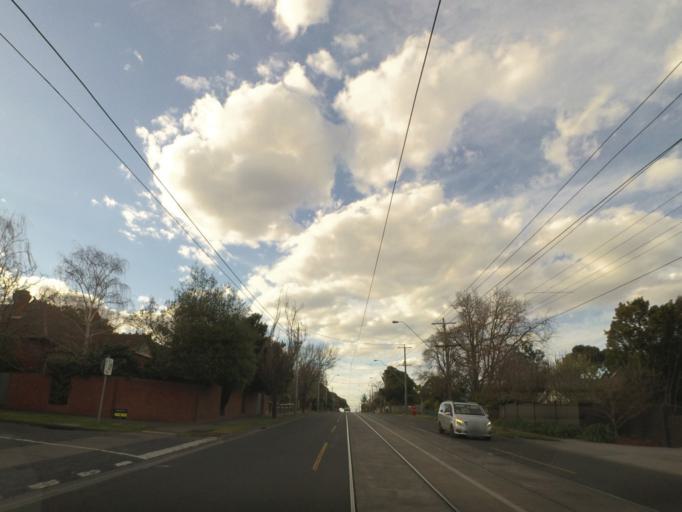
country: AU
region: Victoria
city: Glenferrie
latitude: -37.8391
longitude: 145.0552
